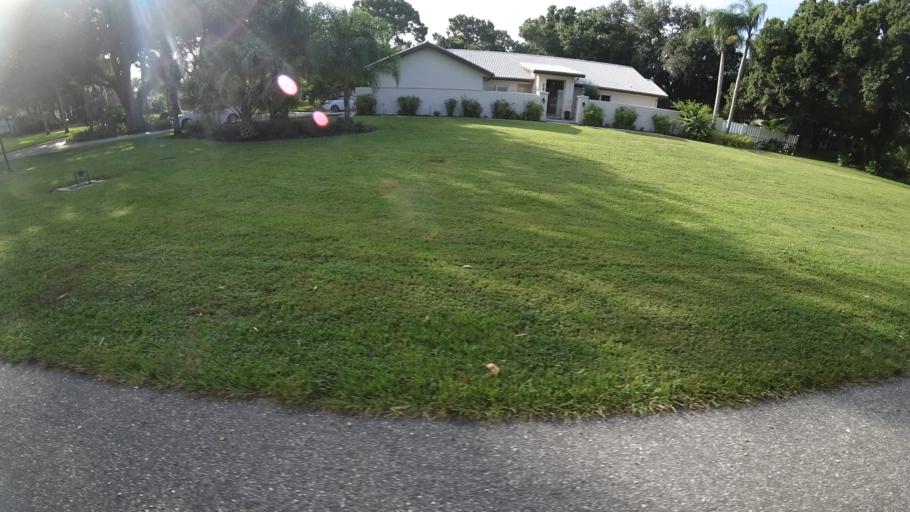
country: US
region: Florida
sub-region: Sarasota County
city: North Sarasota
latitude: 27.4094
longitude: -82.5020
